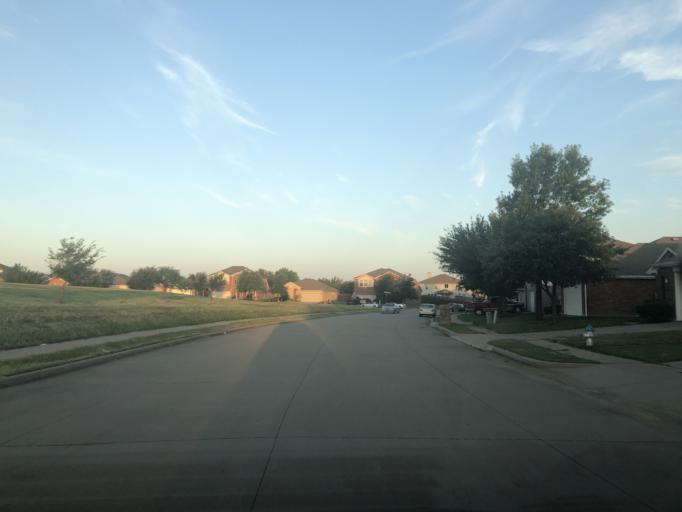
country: US
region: Texas
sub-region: Dallas County
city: Duncanville
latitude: 32.6548
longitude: -96.9751
